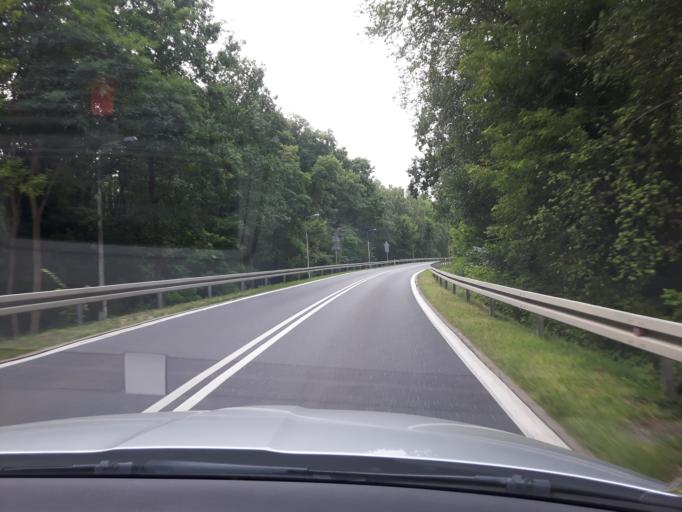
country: PL
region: Masovian Voivodeship
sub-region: Powiat legionowski
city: Wieliszew
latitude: 52.4437
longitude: 20.9944
